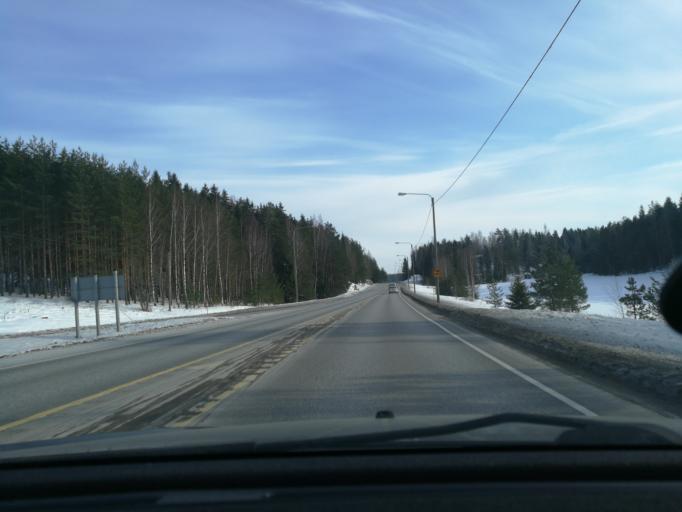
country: FI
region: Uusimaa
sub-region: Helsinki
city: Saukkola
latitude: 60.3836
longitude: 24.0848
